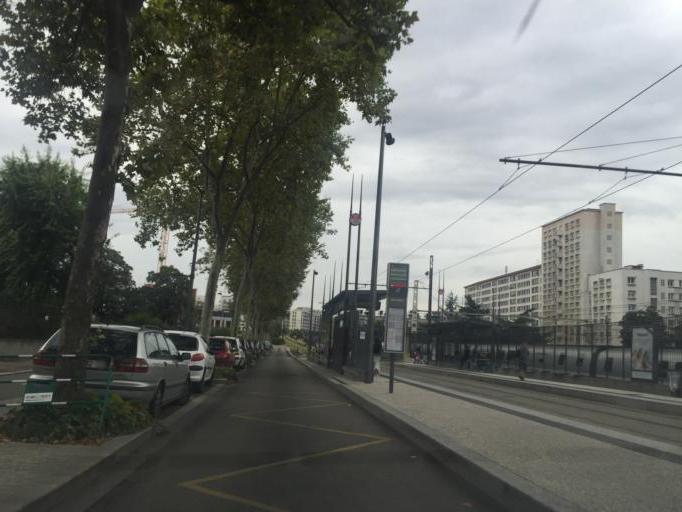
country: FR
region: Rhone-Alpes
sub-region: Departement du Rhone
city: Lyon
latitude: 45.7459
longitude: 4.8592
